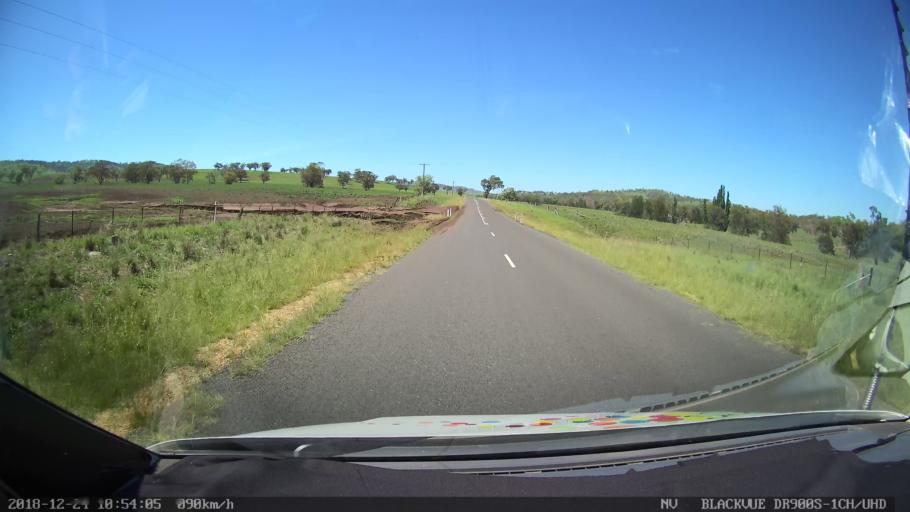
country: AU
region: New South Wales
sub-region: Upper Hunter Shire
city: Merriwa
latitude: -31.9996
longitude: 150.4186
